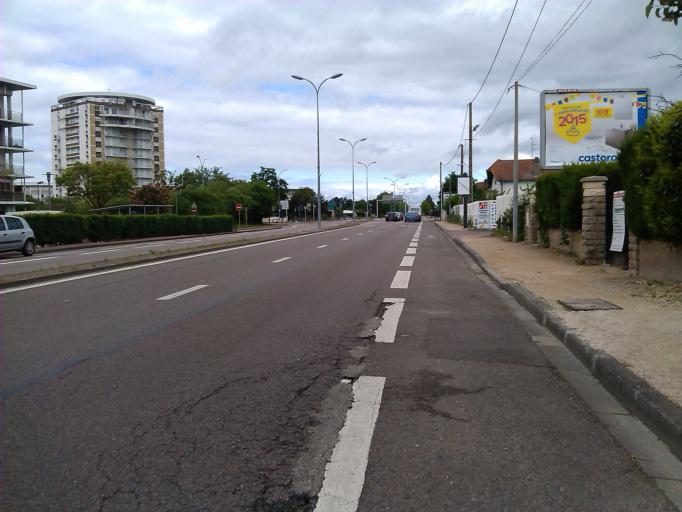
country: FR
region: Bourgogne
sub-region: Departement de Saone-et-Loire
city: Champforgeuil
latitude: 46.8054
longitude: 4.8447
